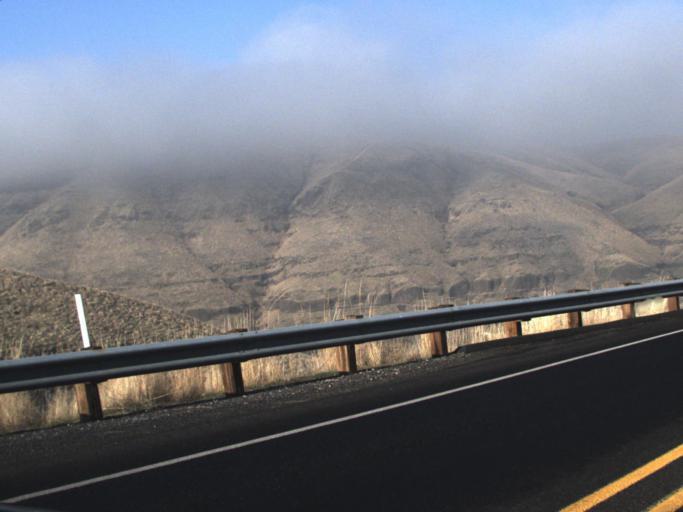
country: US
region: Washington
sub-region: Asotin County
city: Asotin
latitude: 46.3316
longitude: -117.0596
